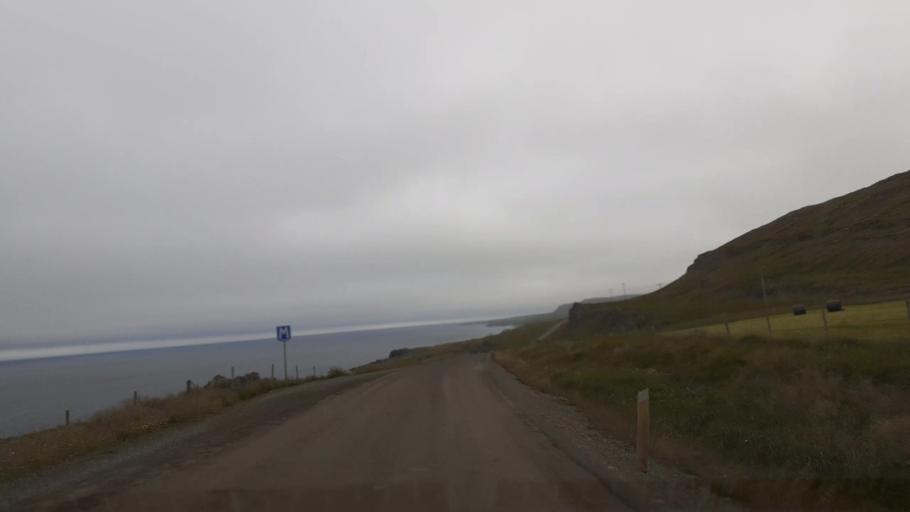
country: IS
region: Northwest
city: Saudarkrokur
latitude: 65.5150
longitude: -20.9713
